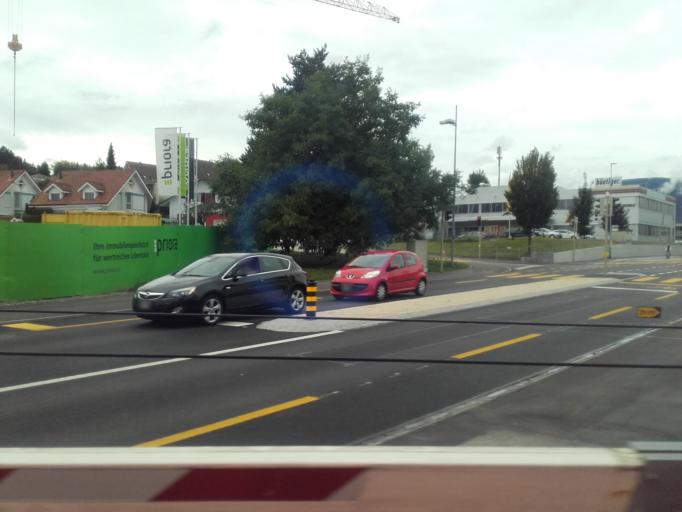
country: CH
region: Solothurn
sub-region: Bezirk Wasseramt
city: Biberist
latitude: 47.1871
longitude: 7.5565
